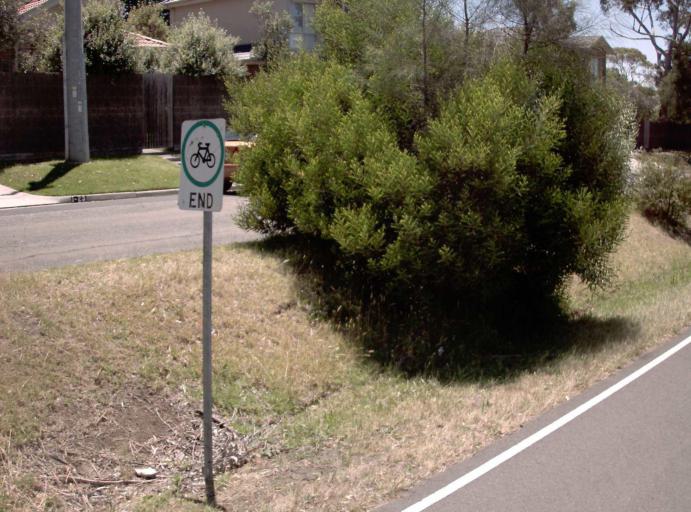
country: AU
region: Victoria
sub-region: Mornington Peninsula
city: Mount Eliza
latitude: -38.1873
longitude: 145.0959
